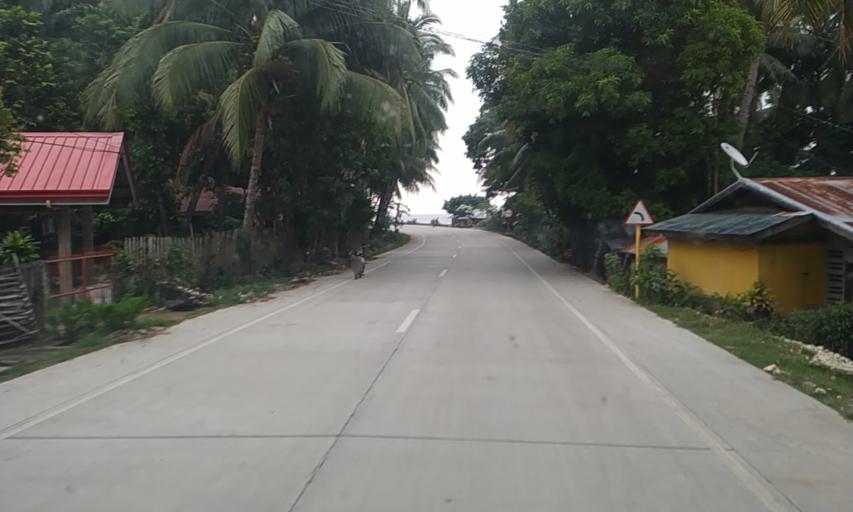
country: PH
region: Central Visayas
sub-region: Province of Negros Oriental
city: Calamba
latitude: 10.1906
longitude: 123.2915
